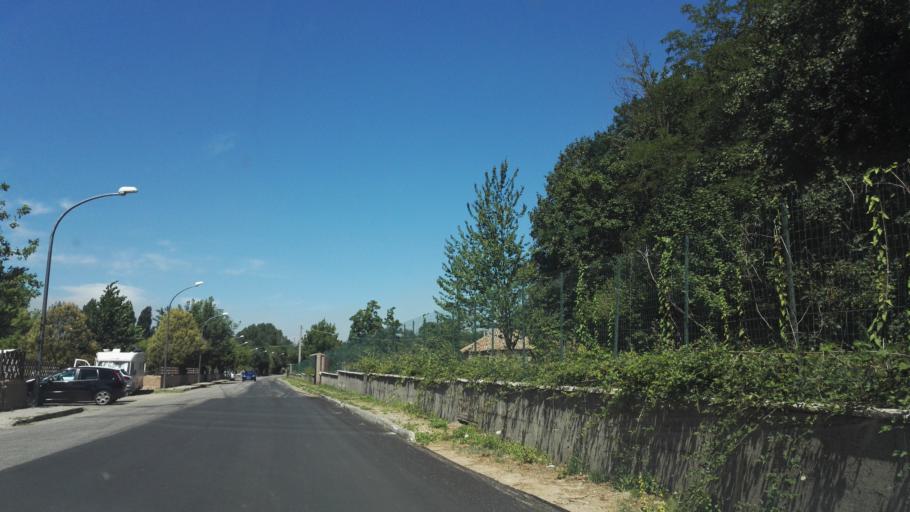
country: IT
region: Calabria
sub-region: Provincia di Vibo-Valentia
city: Serra San Bruno
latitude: 38.5721
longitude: 16.3301
